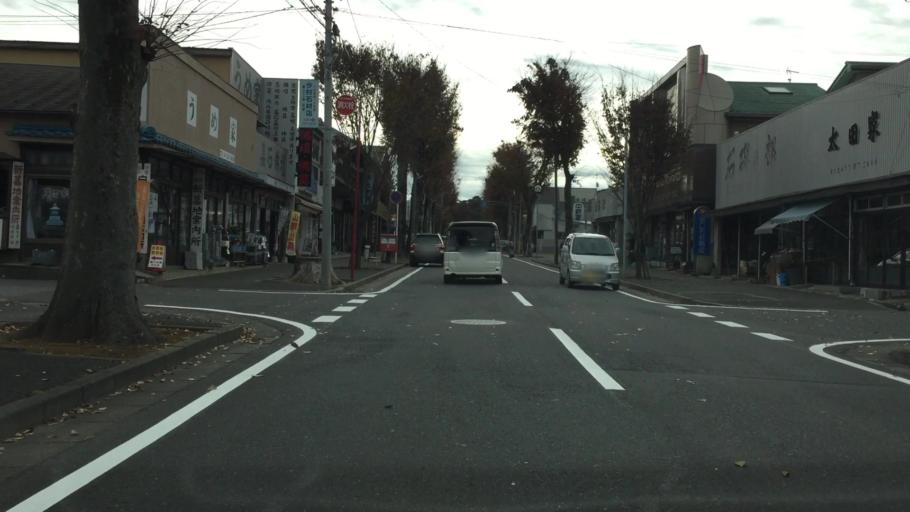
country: JP
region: Chiba
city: Matsudo
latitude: 35.7851
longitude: 139.9458
